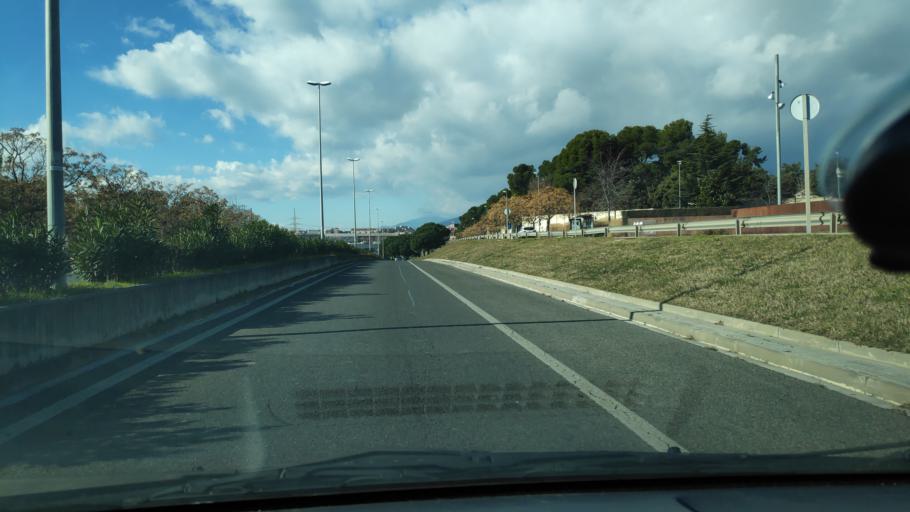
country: ES
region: Catalonia
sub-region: Provincia de Barcelona
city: Terrassa
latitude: 41.5567
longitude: 2.0430
